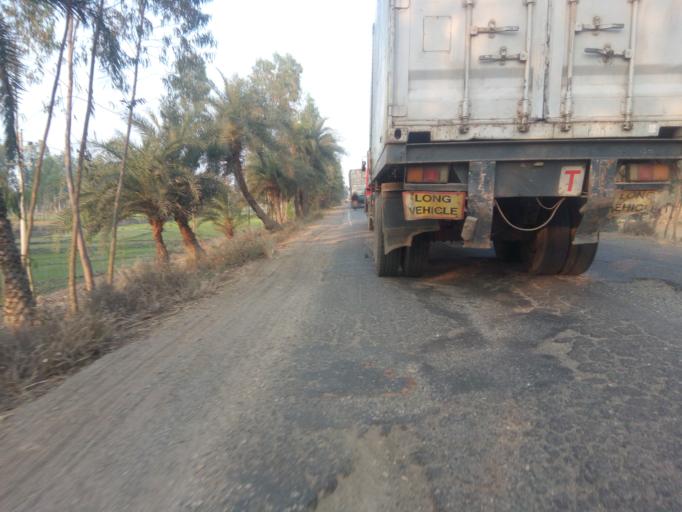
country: BD
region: Rajshahi
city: Par Naogaon
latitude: 24.5462
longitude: 89.1884
